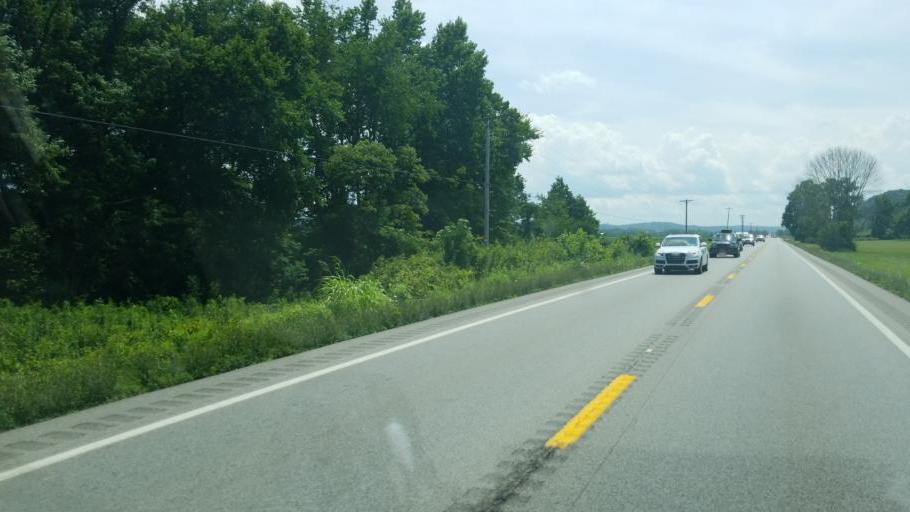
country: US
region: West Virginia
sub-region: Putnam County
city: Buffalo
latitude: 38.6739
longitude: -81.9661
